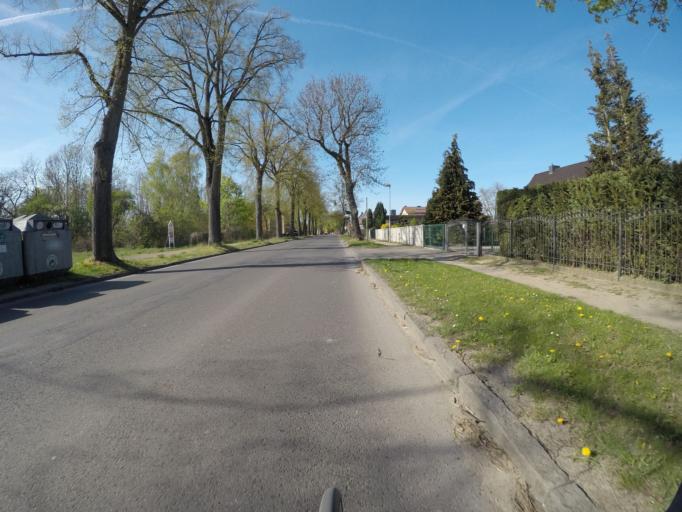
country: DE
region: Brandenburg
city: Rehfelde
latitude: 52.4777
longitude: 13.8526
